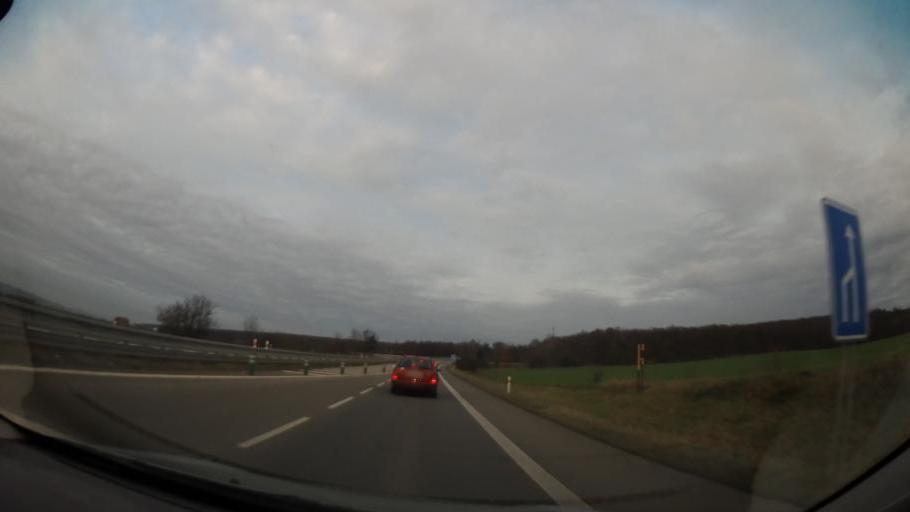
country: CZ
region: South Moravian
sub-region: Okres Brno-Venkov
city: Rosice
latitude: 49.1916
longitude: 16.4188
